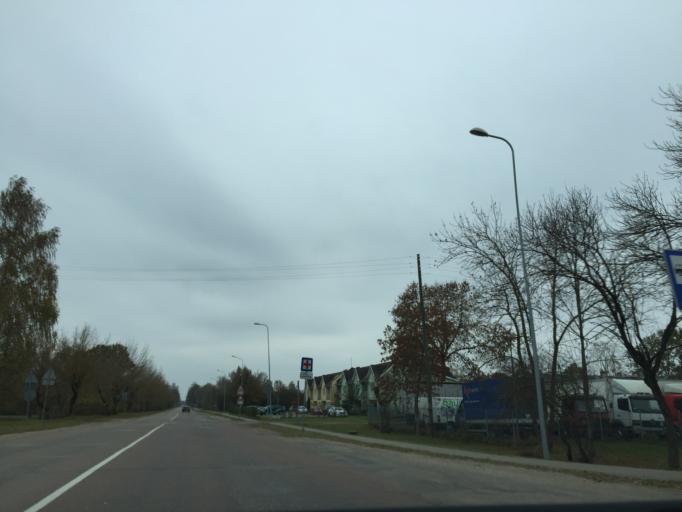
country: LV
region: Marupe
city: Marupe
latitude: 56.8826
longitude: 24.0690
